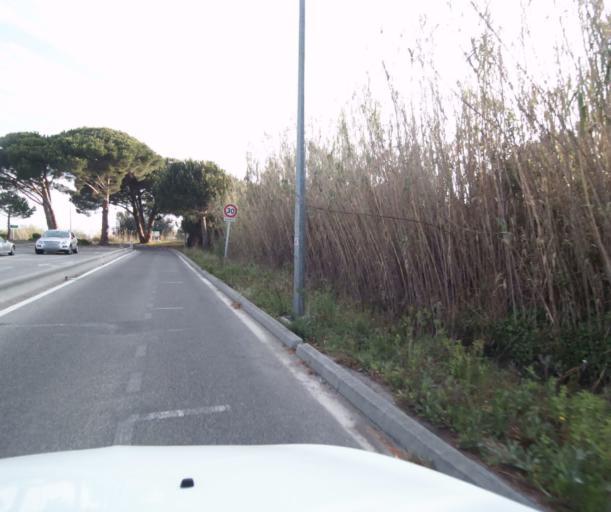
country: FR
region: Provence-Alpes-Cote d'Azur
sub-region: Departement du Var
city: Hyeres
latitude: 43.0935
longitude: 6.1602
